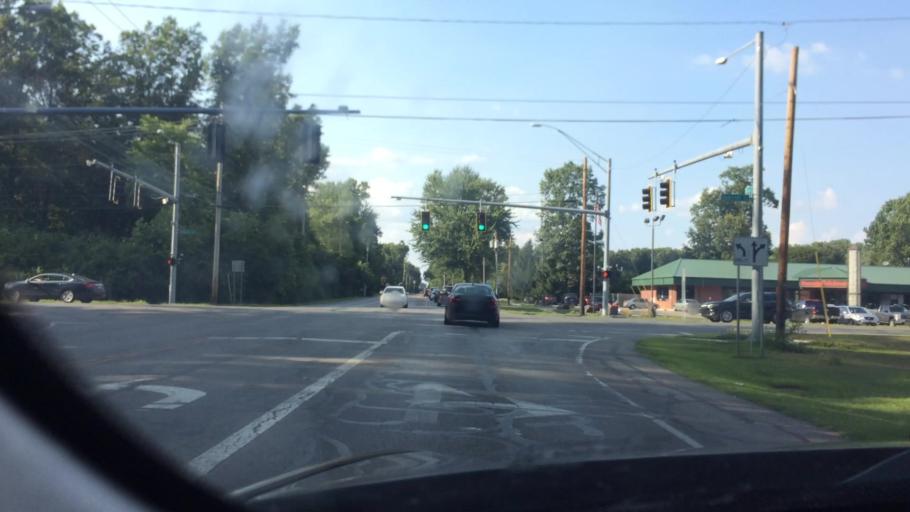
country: US
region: Ohio
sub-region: Lucas County
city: Holland
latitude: 41.6591
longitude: -83.7222
